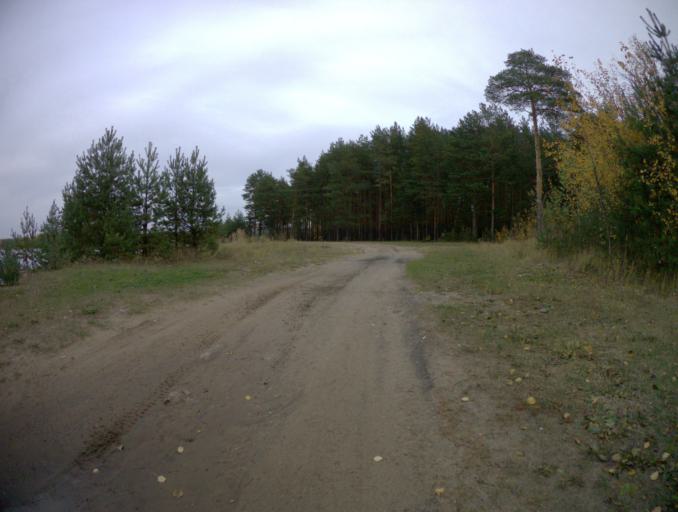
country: RU
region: Vladimir
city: Golovino
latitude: 56.0350
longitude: 40.4157
